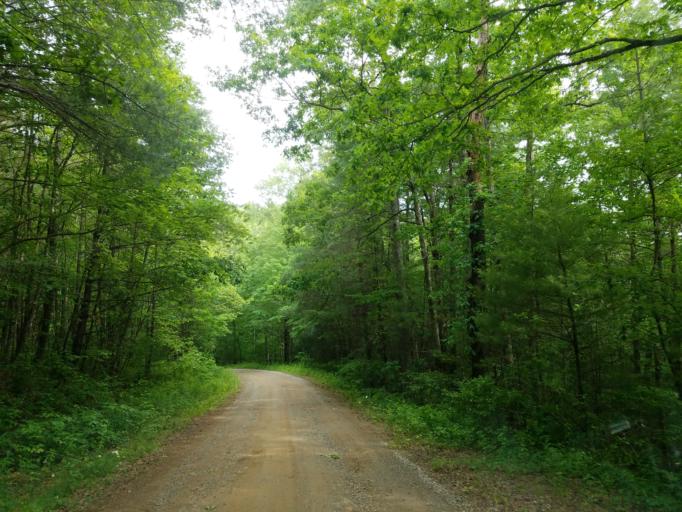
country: US
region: Georgia
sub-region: Union County
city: Blairsville
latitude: 34.7569
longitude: -84.0025
